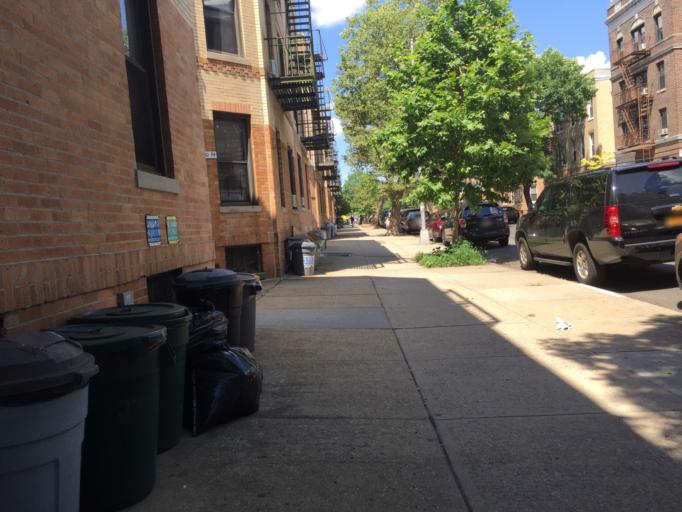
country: US
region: New York
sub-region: Queens County
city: Long Island City
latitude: 40.7644
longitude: -73.9214
